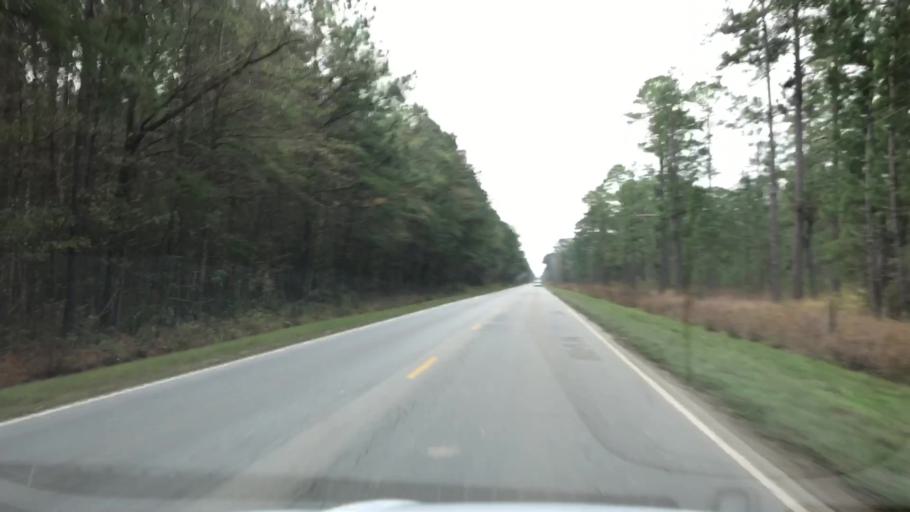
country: US
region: South Carolina
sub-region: Jasper County
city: Ridgeland
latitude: 32.3813
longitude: -80.9105
